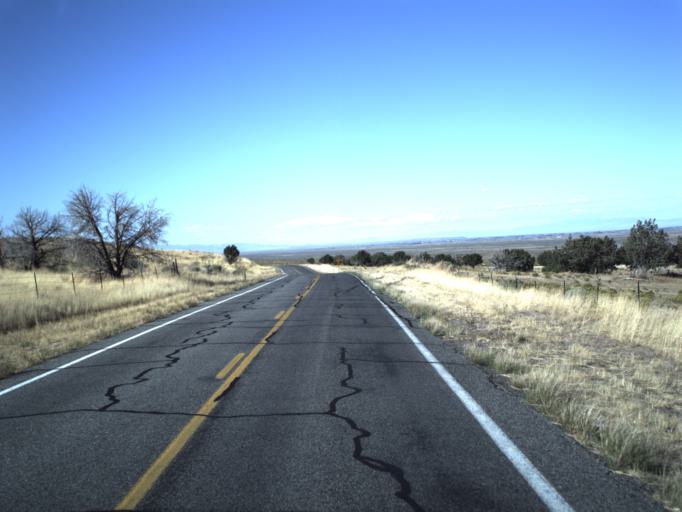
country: US
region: Utah
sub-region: Millard County
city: Delta
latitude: 39.3593
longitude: -112.3566
